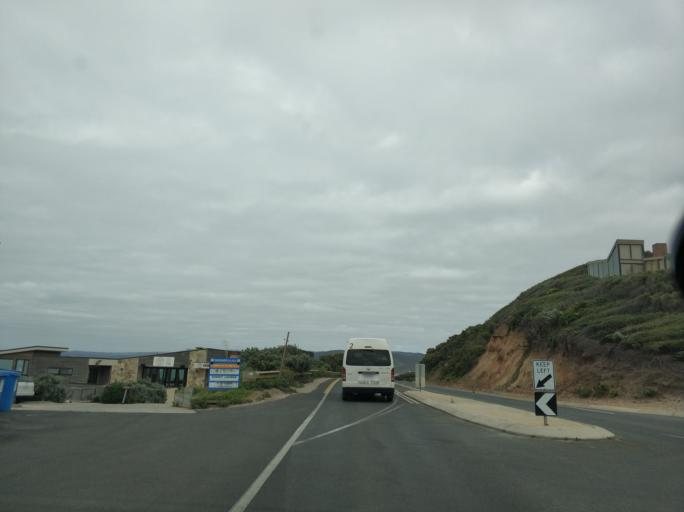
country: AU
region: Victoria
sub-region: Surf Coast
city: Anglesea
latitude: -38.4681
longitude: 144.0849
